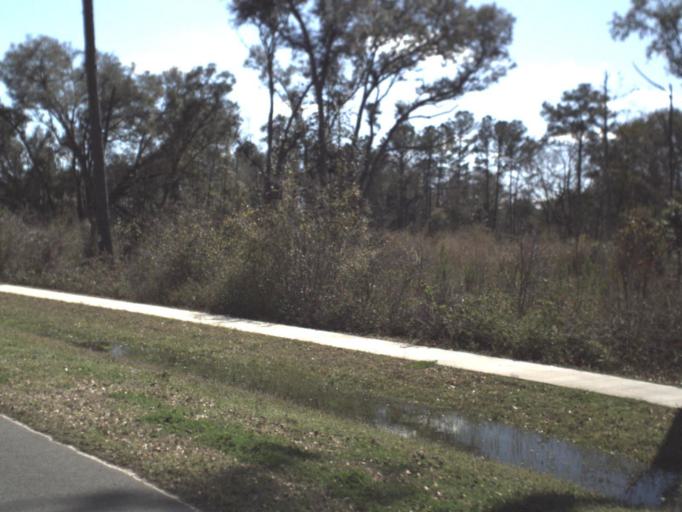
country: US
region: Florida
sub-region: Gadsden County
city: Gretna
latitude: 30.6123
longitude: -84.6602
